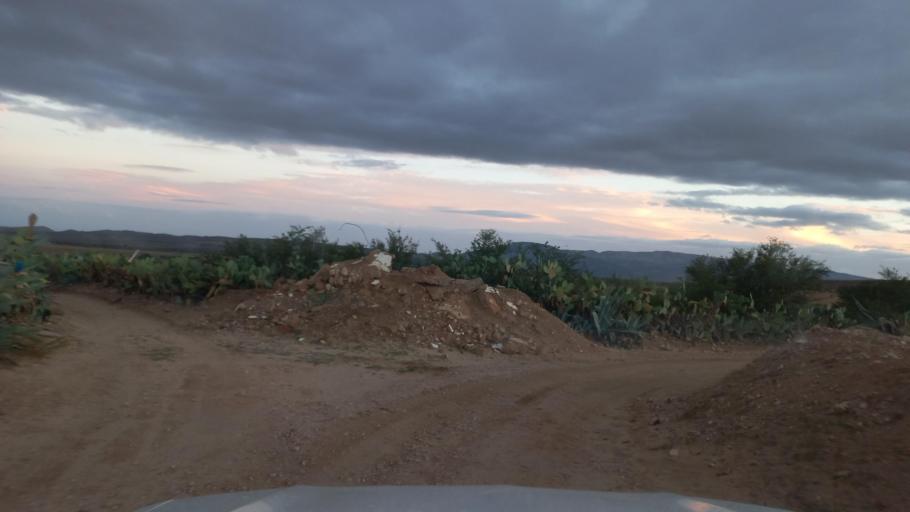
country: TN
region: Al Qasrayn
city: Kasserine
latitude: 35.2554
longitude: 8.9360
